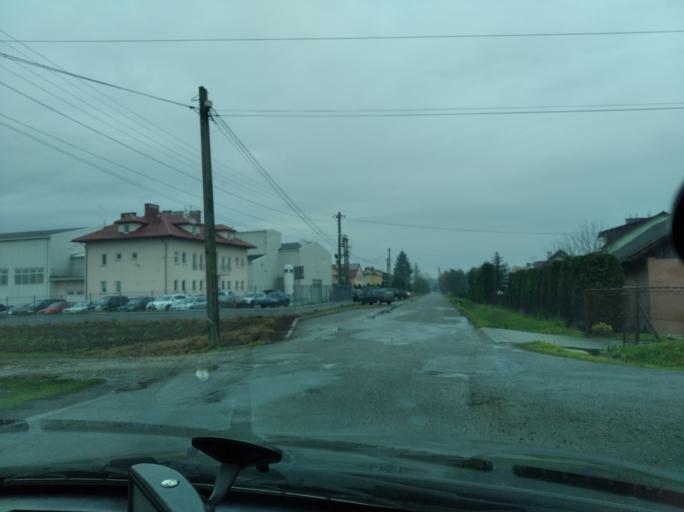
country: PL
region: Subcarpathian Voivodeship
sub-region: Powiat strzyzowski
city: Babica
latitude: 49.9251
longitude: 21.8618
